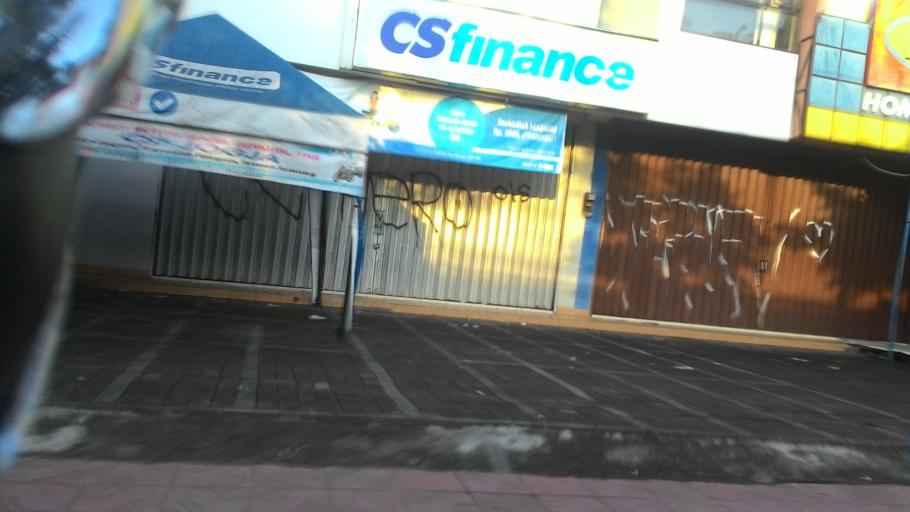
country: ID
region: Daerah Istimewa Yogyakarta
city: Yogyakarta
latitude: -7.7984
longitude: 110.3694
